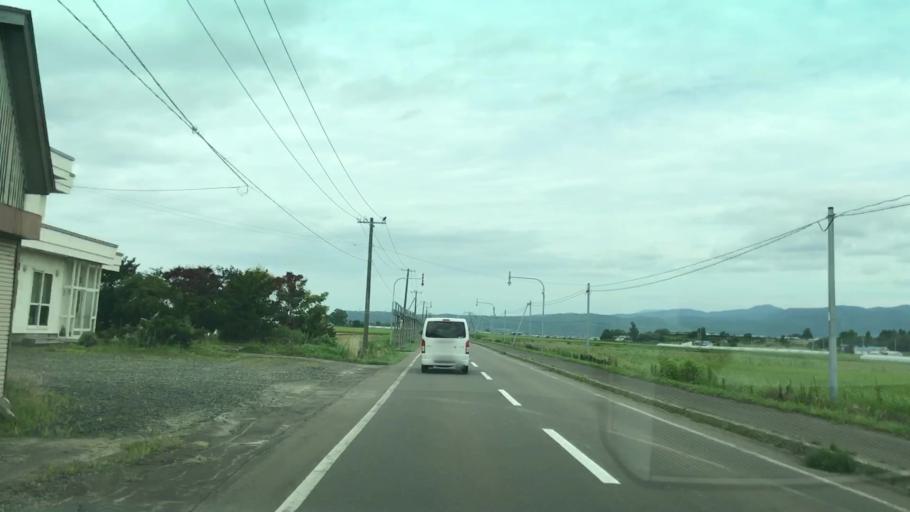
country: JP
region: Hokkaido
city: Iwanai
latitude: 42.9941
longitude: 140.5995
